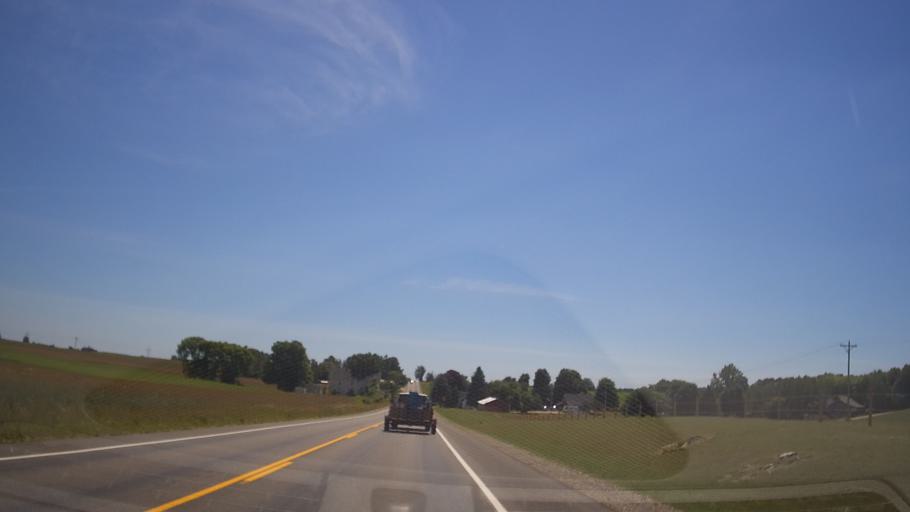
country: US
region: Michigan
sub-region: Grand Traverse County
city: Kingsley
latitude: 44.6168
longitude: -85.6966
